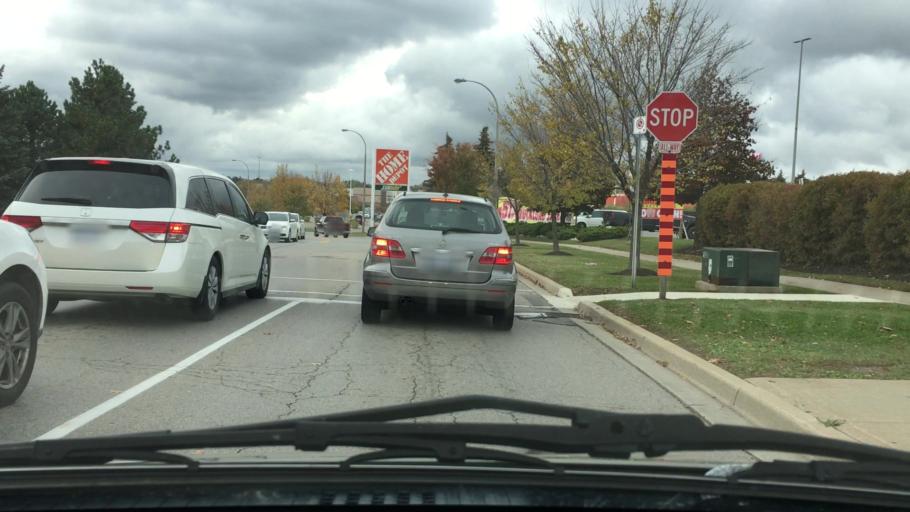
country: CA
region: Ontario
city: Ancaster
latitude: 43.2292
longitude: -79.9420
